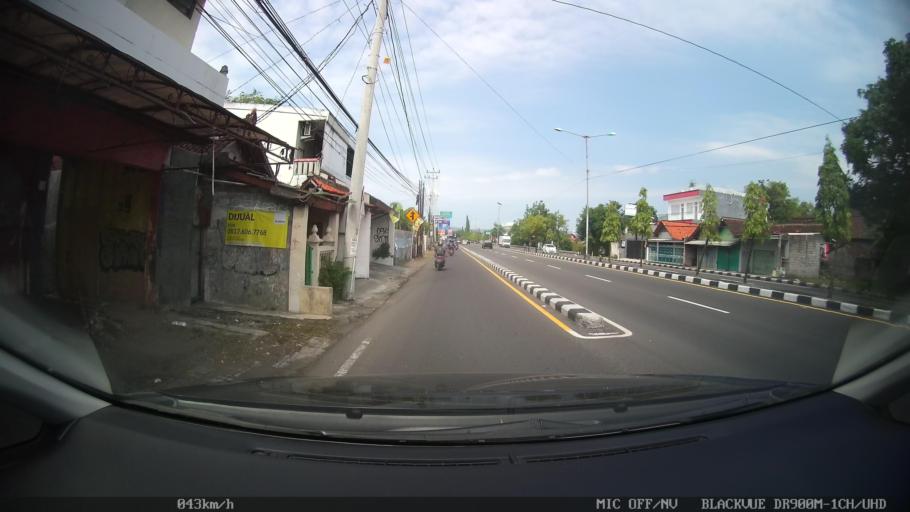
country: ID
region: Daerah Istimewa Yogyakarta
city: Depok
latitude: -7.7656
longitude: 110.4265
